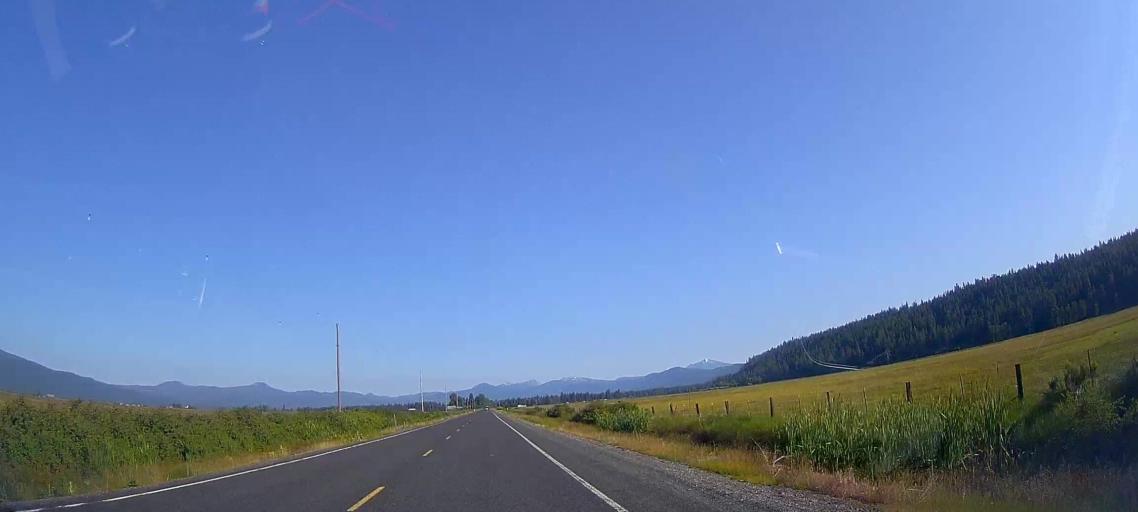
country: US
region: Oregon
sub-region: Klamath County
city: Klamath Falls
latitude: 42.6549
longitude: -121.9591
